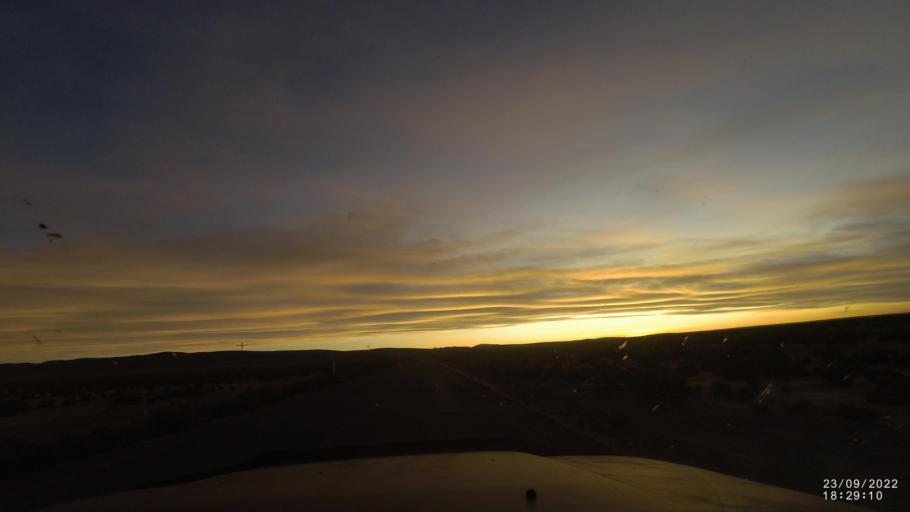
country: BO
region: Oruro
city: Challapata
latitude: -19.3430
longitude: -67.1882
